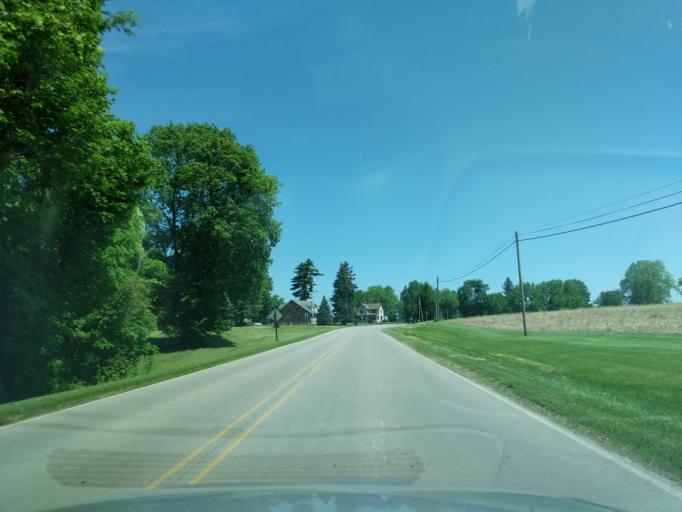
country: US
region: Indiana
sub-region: Huntington County
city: Huntington
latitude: 40.8956
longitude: -85.4842
